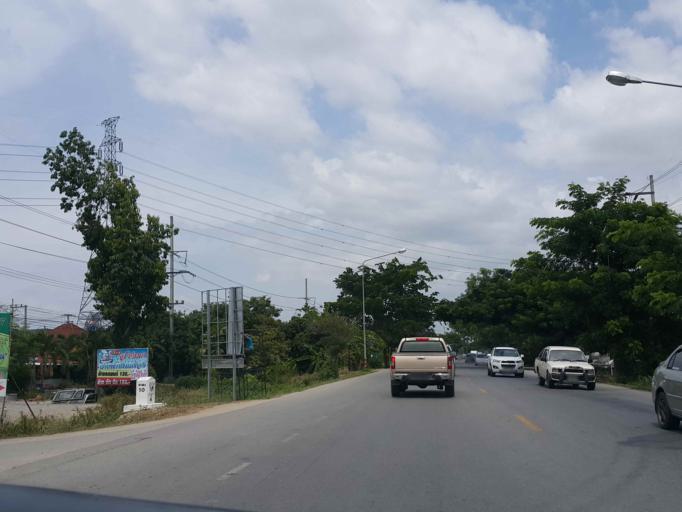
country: TH
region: Chiang Mai
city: Saraphi
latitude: 18.7206
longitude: 99.0024
